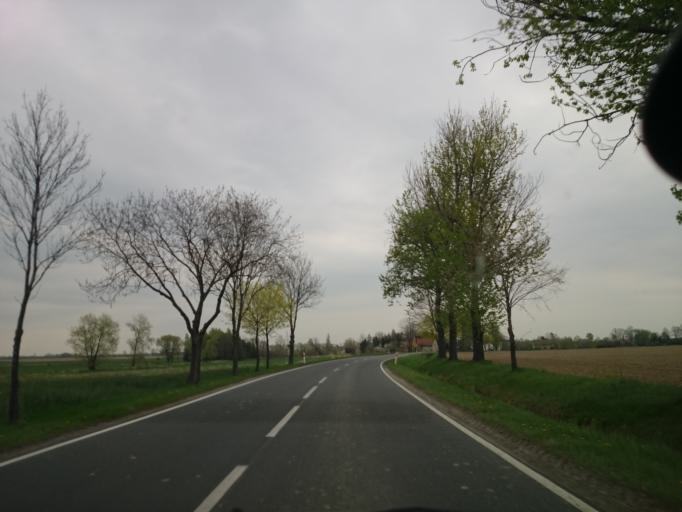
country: PL
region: Opole Voivodeship
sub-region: Powiat prudnicki
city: Moszczanka
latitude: 50.3253
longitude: 17.4625
